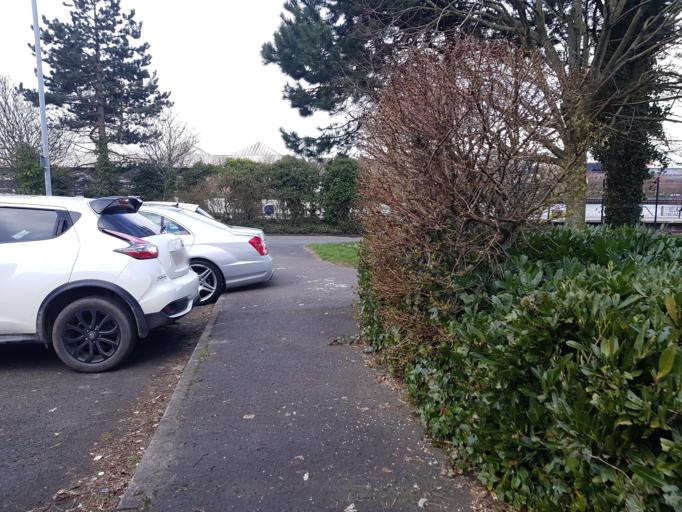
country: GB
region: Northern Ireland
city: Londonderry County Borough
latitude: 54.9922
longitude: -7.3131
